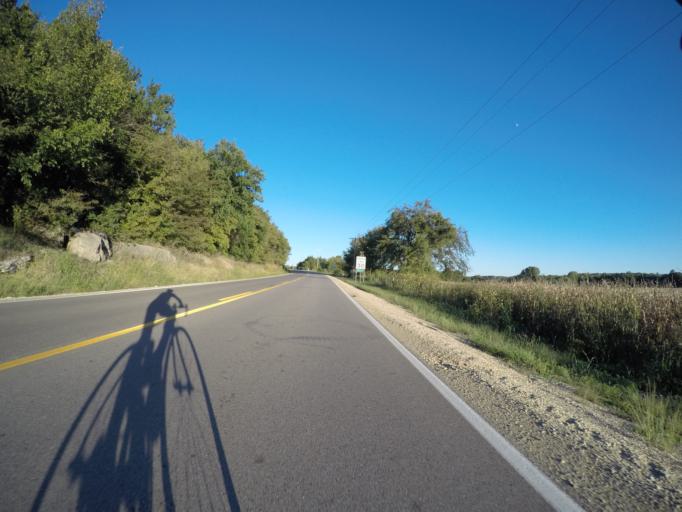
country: US
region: Kansas
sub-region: Riley County
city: Ogden
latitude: 39.2263
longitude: -96.7137
